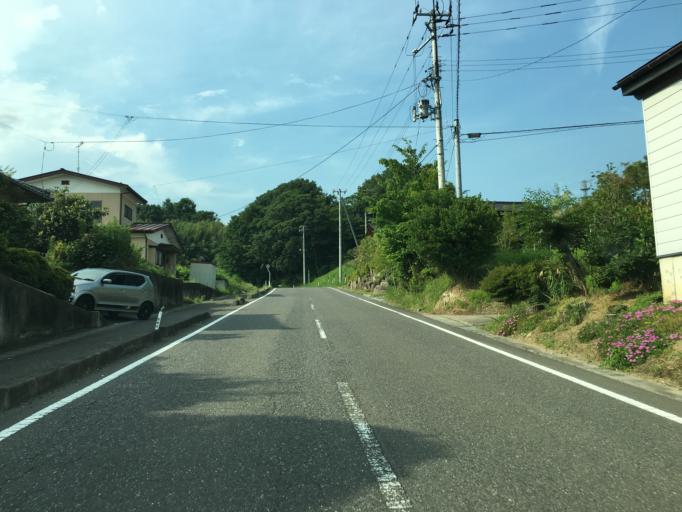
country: JP
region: Fukushima
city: Miharu
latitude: 37.4277
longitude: 140.4530
